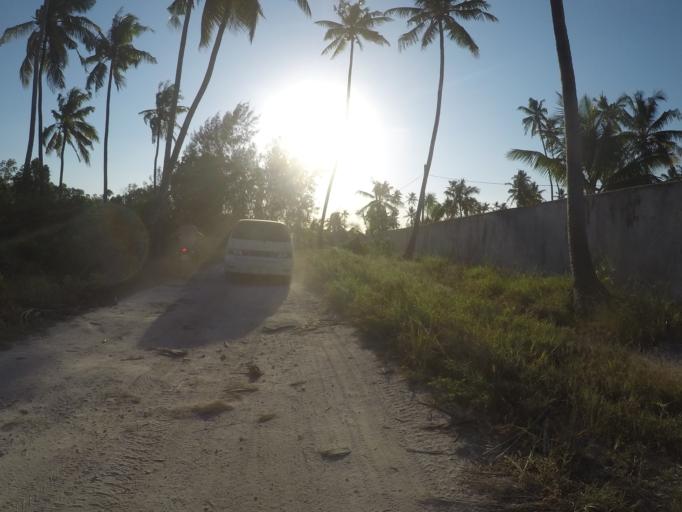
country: TZ
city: Kiwengwa
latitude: -6.1436
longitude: 39.4916
